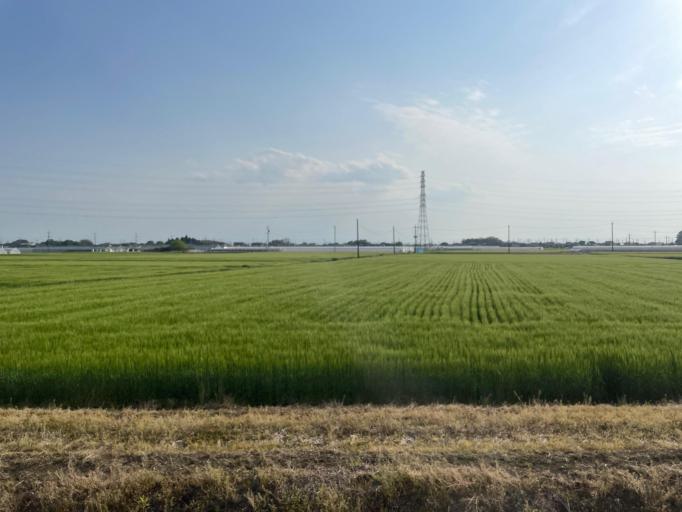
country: JP
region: Tochigi
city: Ashikaga
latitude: 36.2939
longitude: 139.4670
